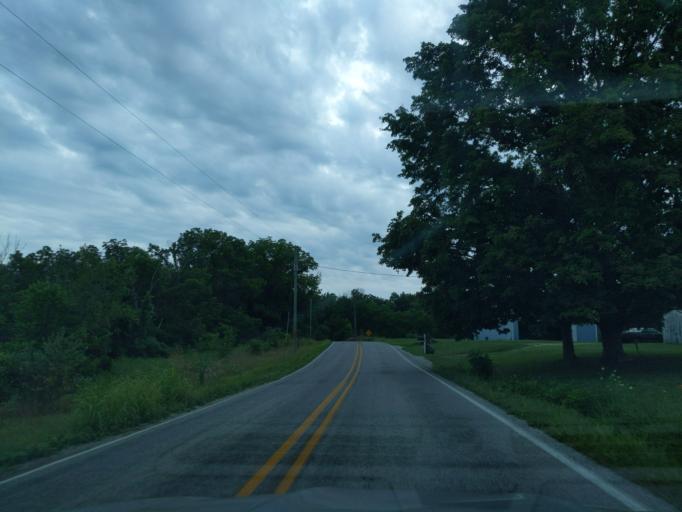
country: US
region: Indiana
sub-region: Ripley County
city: Batesville
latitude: 39.2010
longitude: -85.1996
